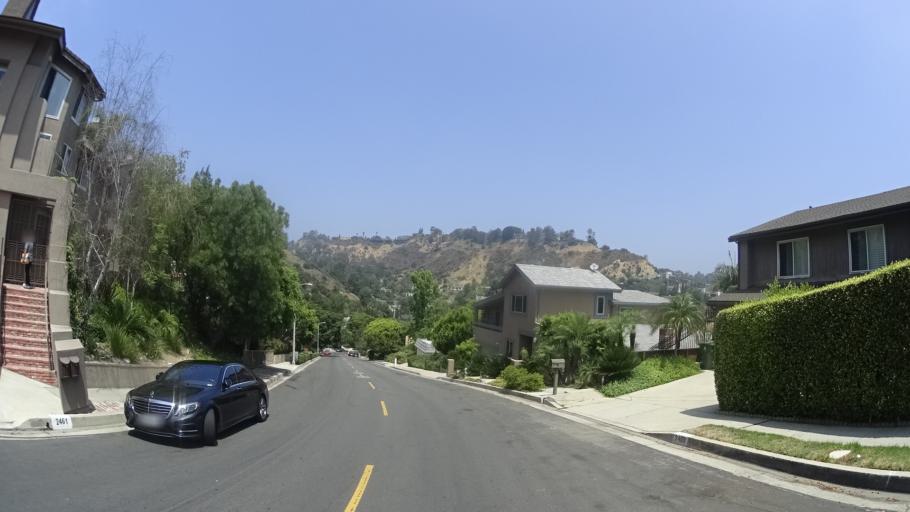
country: US
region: California
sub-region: Los Angeles County
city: West Hollywood
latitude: 34.1150
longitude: -118.3626
